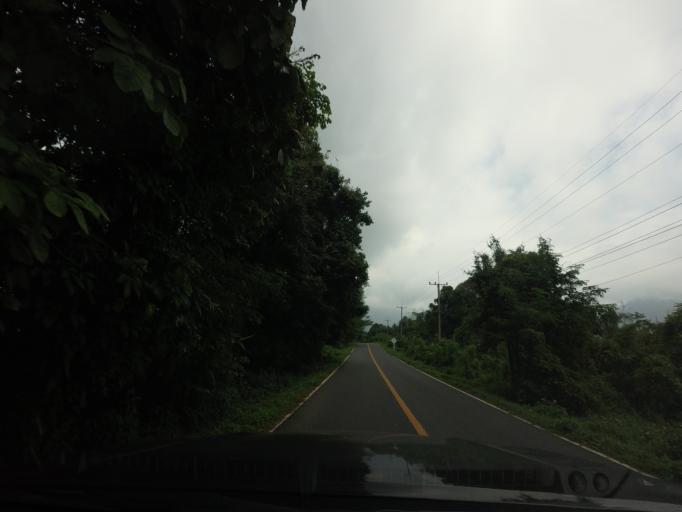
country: TH
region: Nan
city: Pua
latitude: 19.1879
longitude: 101.0357
